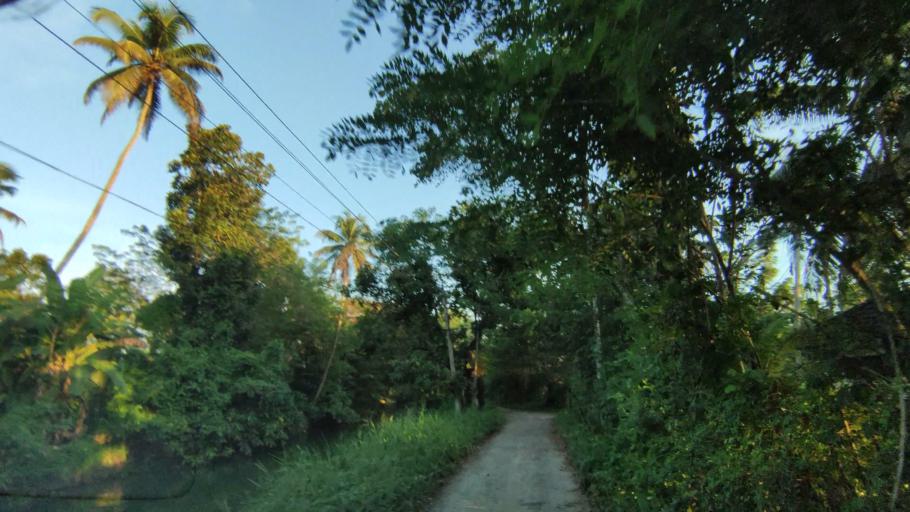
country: IN
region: Kerala
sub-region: Kottayam
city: Kottayam
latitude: 9.6336
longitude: 76.4789
